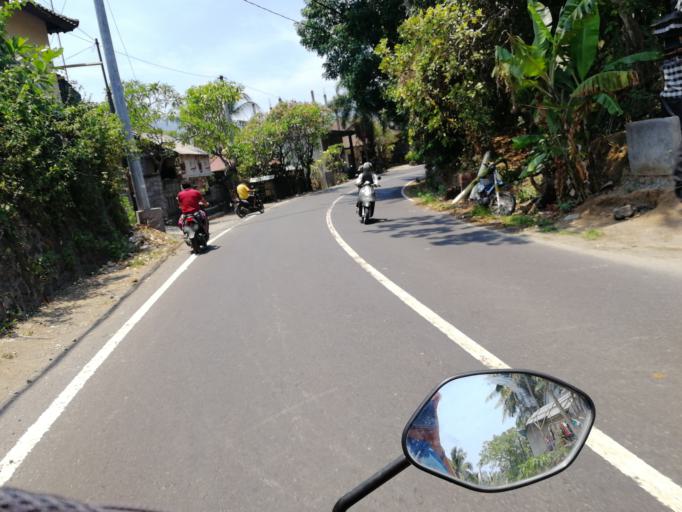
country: ID
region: Bali
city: Padangbai
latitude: -8.5243
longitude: 115.5017
